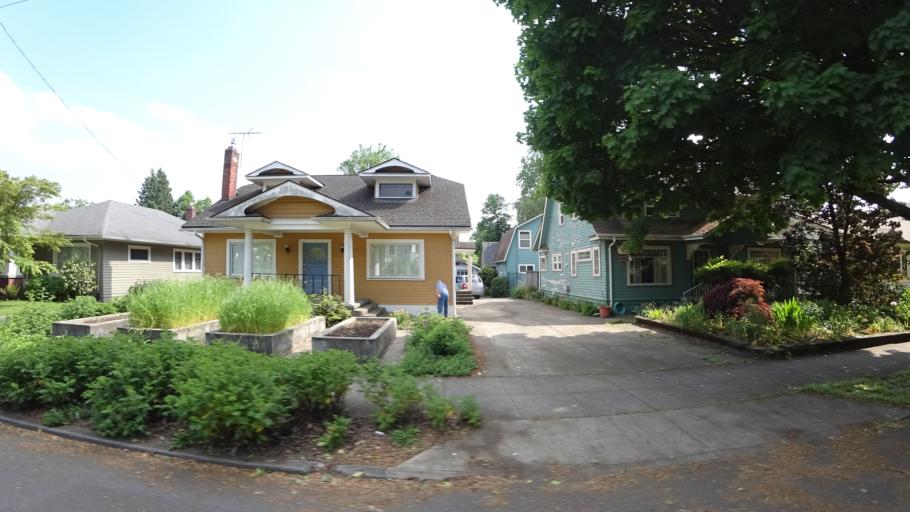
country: US
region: Oregon
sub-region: Multnomah County
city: Portland
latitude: 45.5193
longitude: -122.6277
